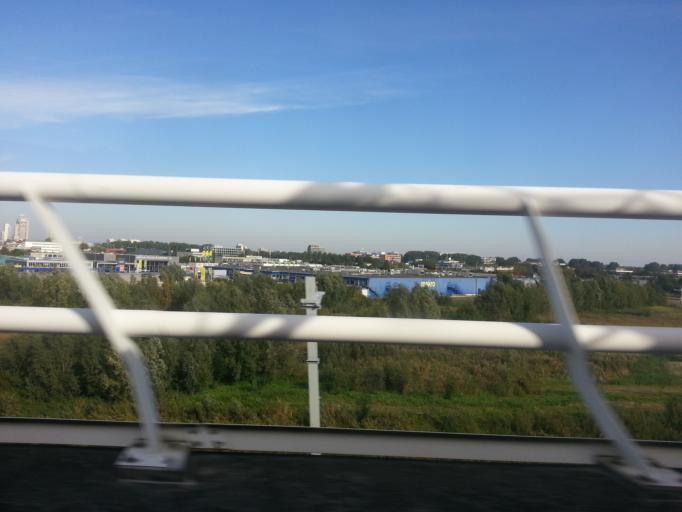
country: NL
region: North Holland
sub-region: Gemeente Ouder-Amstel
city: Duivendrecht
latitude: 52.3223
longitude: 4.9258
